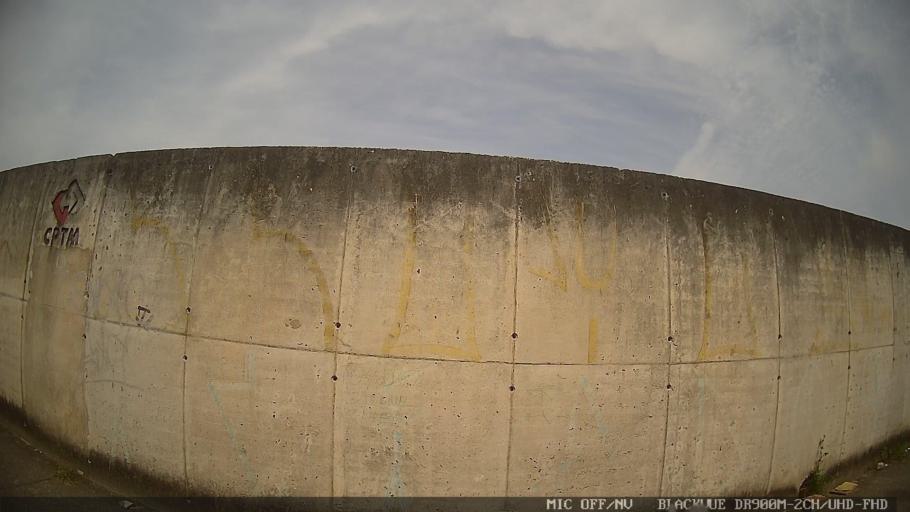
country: BR
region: Sao Paulo
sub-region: Itaquaquecetuba
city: Itaquaquecetuba
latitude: -23.4903
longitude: -46.3358
